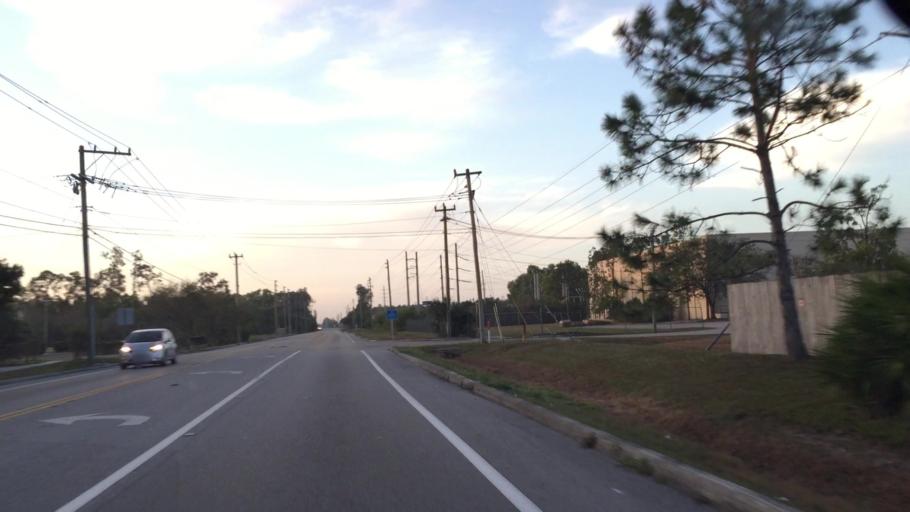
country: US
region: Florida
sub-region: Lee County
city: Pine Manor
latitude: 26.5734
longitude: -81.8472
